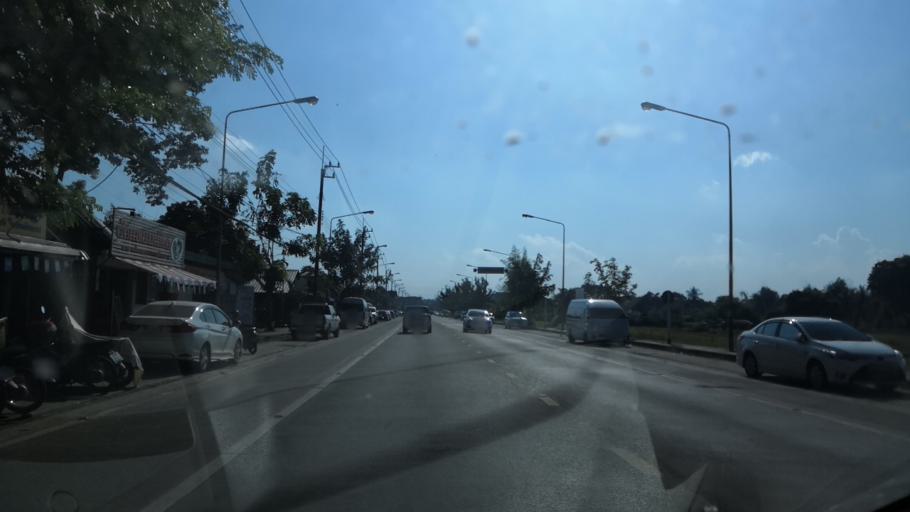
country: TH
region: Chiang Rai
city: Chiang Rai
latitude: 19.9321
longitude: 99.8403
